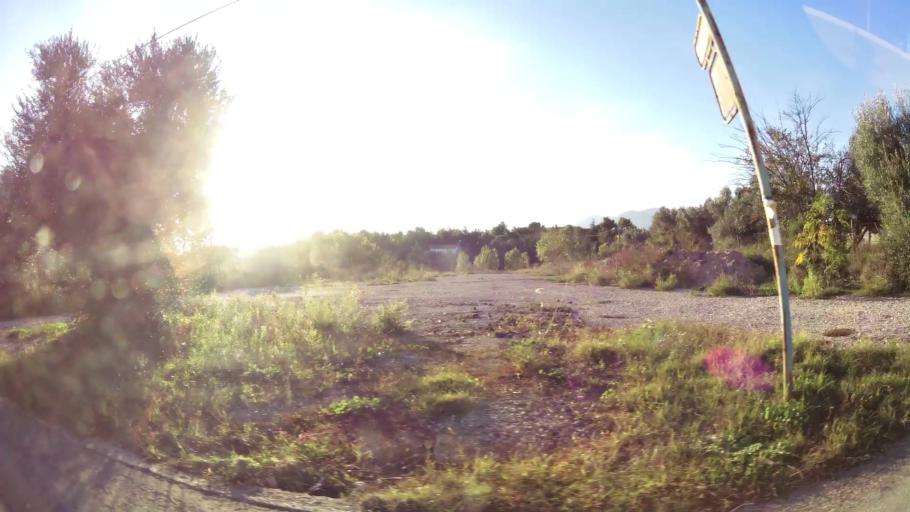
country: GR
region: Attica
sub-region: Nomarchia Anatolikis Attikis
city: Kryoneri
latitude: 38.1298
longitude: 23.8308
